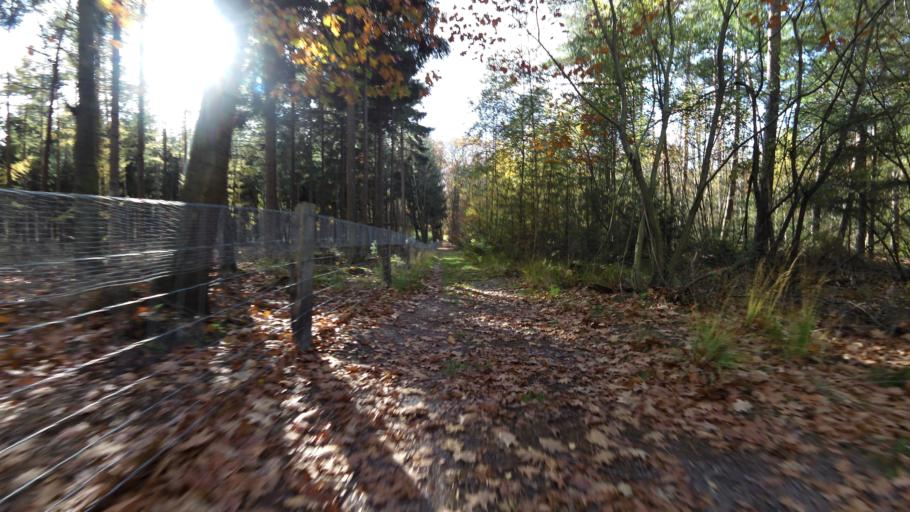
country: NL
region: Gelderland
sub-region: Gemeente Nunspeet
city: Nunspeet
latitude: 52.3533
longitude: 5.8104
